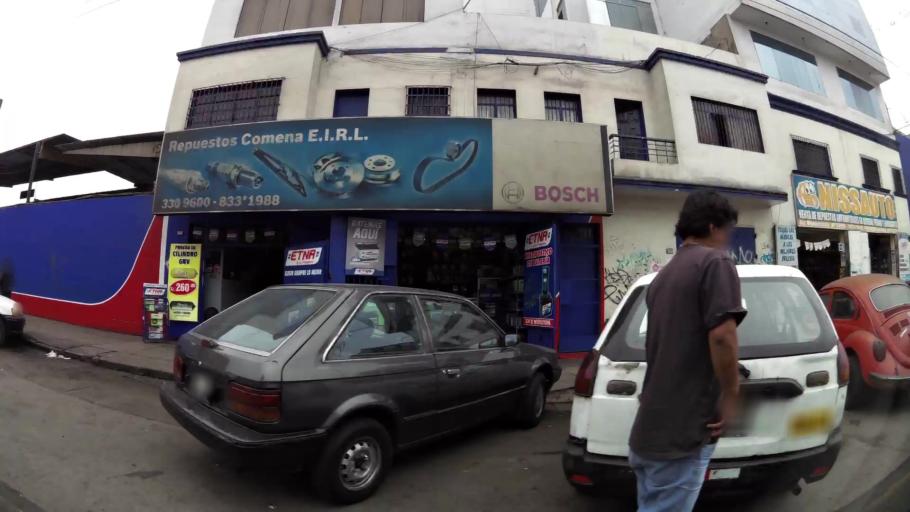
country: PE
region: Lima
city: Lima
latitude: -12.0556
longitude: -77.0535
